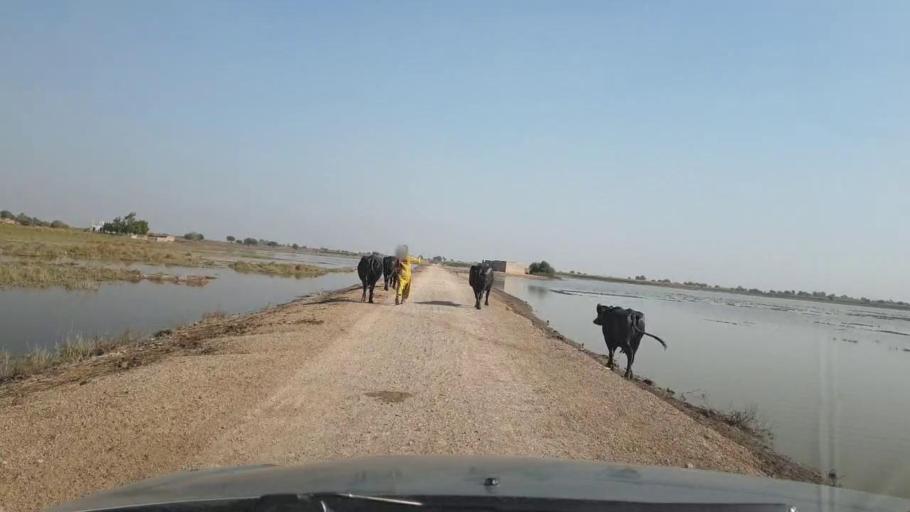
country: PK
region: Sindh
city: Tando Muhammad Khan
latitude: 25.1147
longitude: 68.5907
